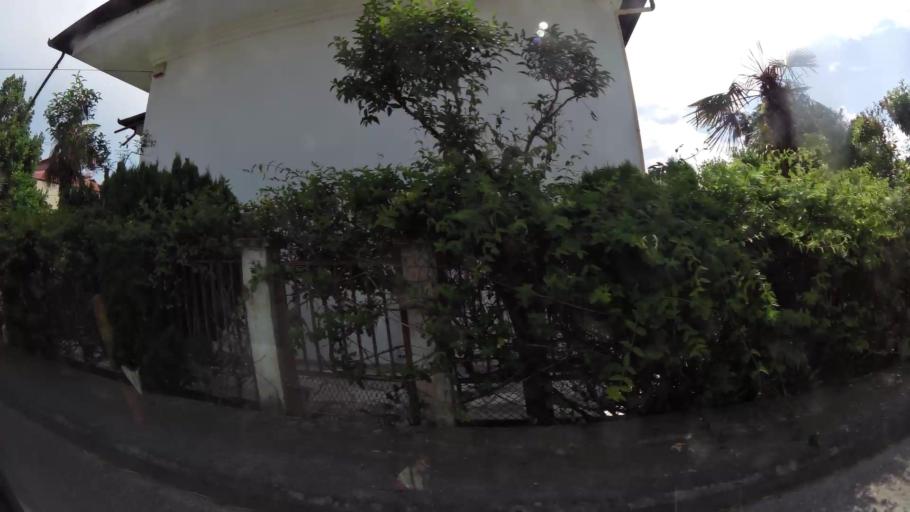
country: GR
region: Central Macedonia
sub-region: Nomos Pierias
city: Korinos
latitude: 40.3205
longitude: 22.5901
